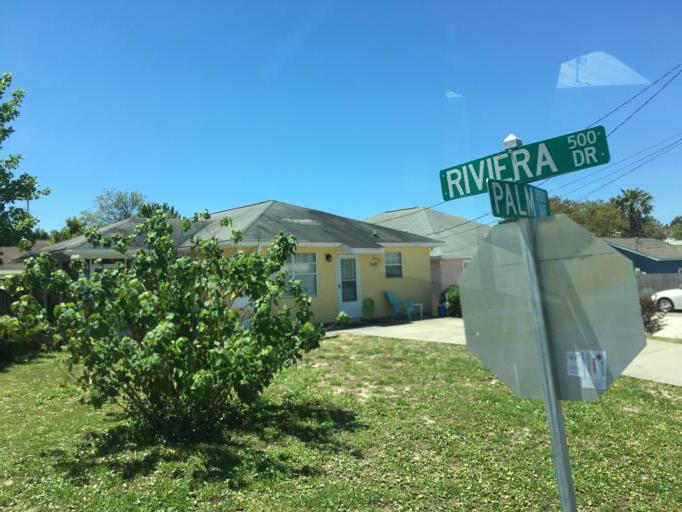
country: US
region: Florida
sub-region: Bay County
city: Laguna Beach
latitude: 30.2573
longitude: -85.9524
